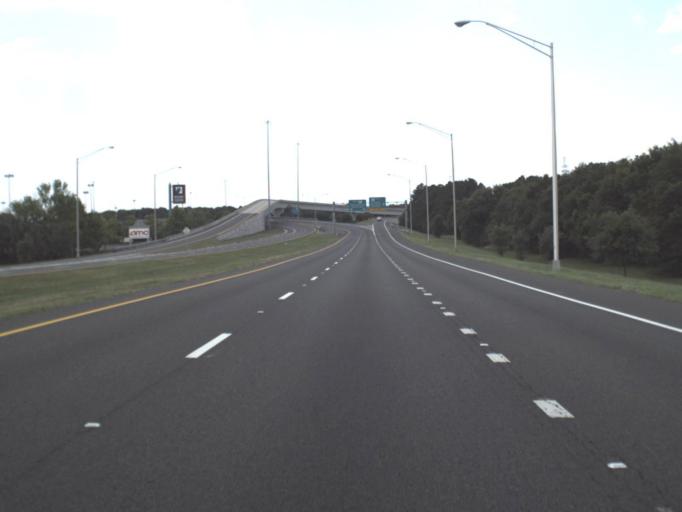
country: US
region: Florida
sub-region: Duval County
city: Jacksonville
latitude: 30.3278
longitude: -81.5558
